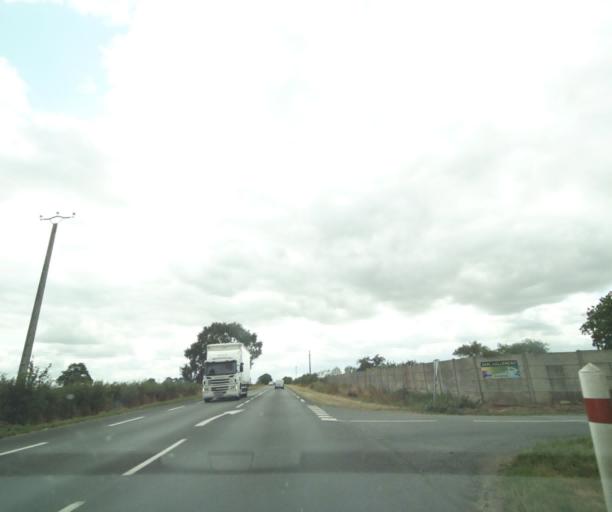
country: FR
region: Pays de la Loire
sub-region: Departement de Maine-et-Loire
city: Le Longeron
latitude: 47.0530
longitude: -1.0550
